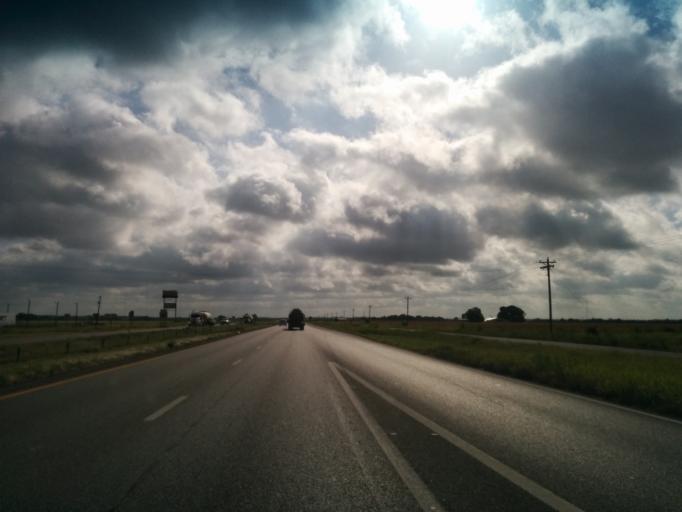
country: US
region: Texas
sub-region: Guadalupe County
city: Marion
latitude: 29.5198
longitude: -98.1364
